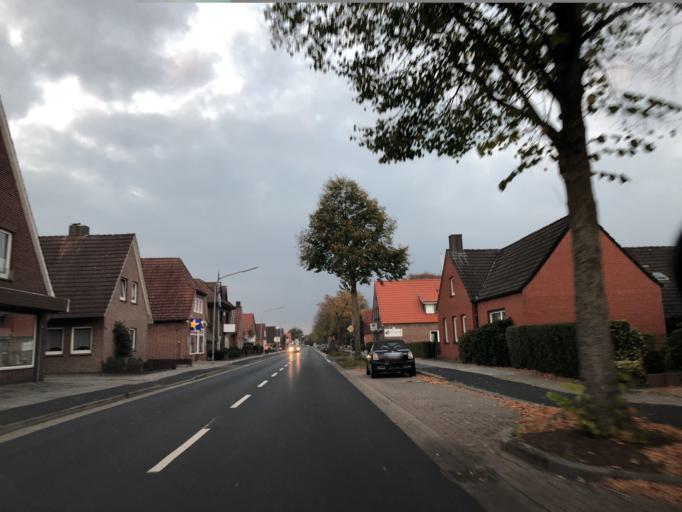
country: DE
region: Lower Saxony
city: Papenburg
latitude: 53.0735
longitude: 7.4187
